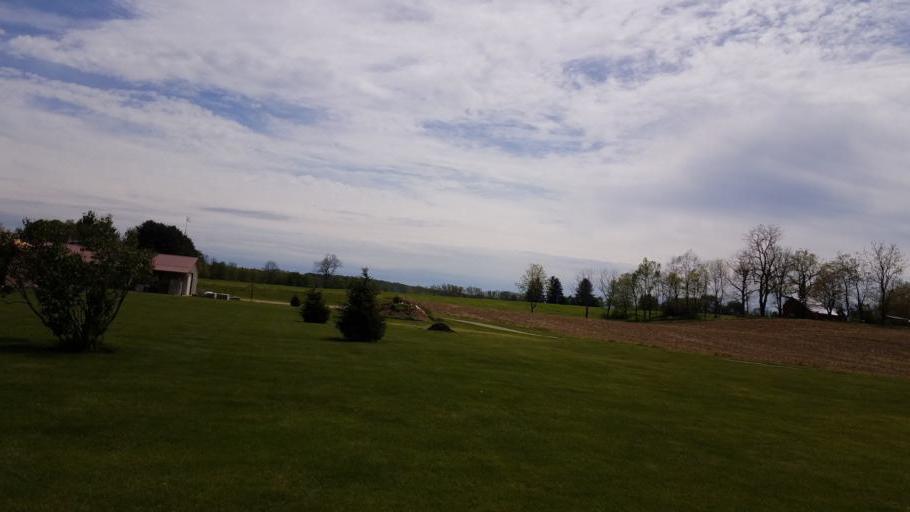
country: US
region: Ohio
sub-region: Knox County
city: Gambier
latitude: 40.3924
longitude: -82.3509
